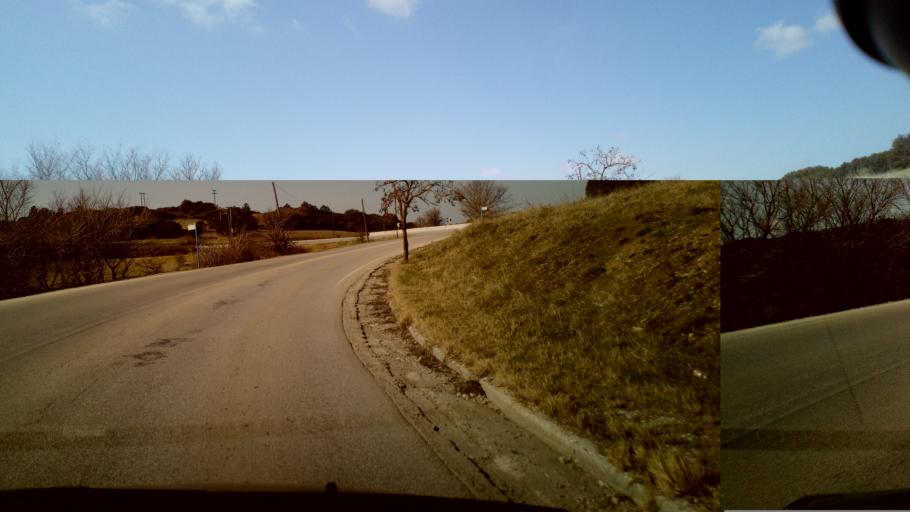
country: GR
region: Central Macedonia
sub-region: Nomos Thessalonikis
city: Chortiatis
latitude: 40.6177
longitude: 23.0631
